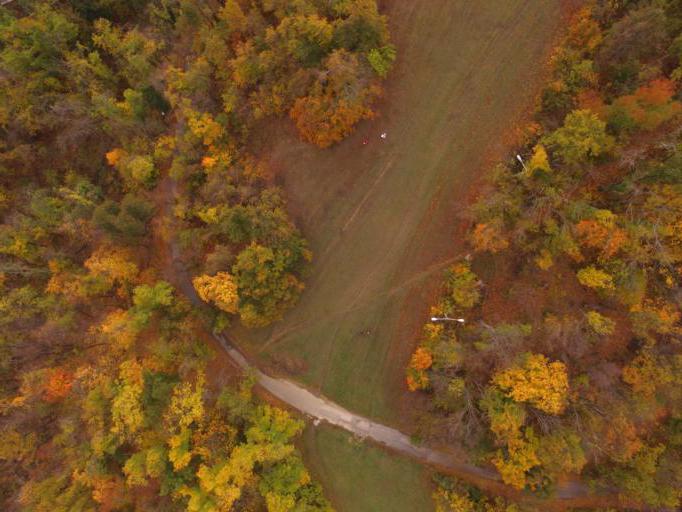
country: HU
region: Pest
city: Budakeszi
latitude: 47.5048
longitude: 18.9713
